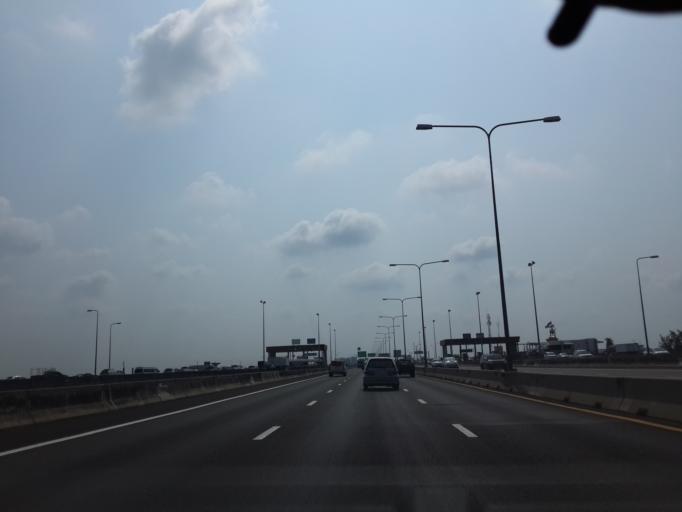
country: TH
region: Bangkok
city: Bang Na
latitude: 13.6474
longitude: 100.6867
